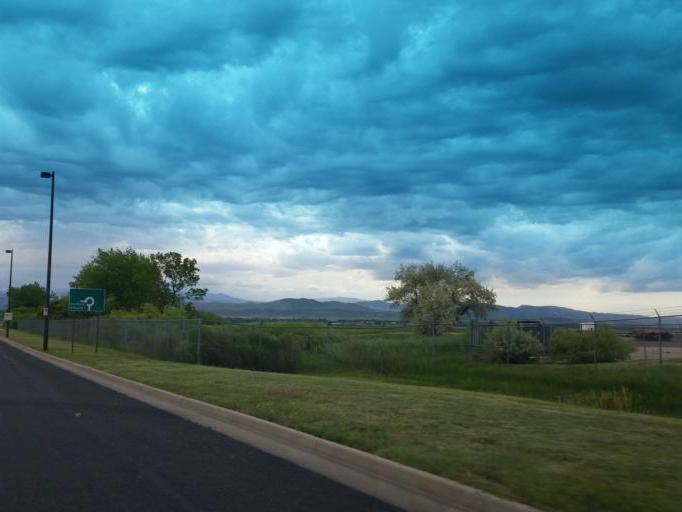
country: US
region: Colorado
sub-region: Larimer County
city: Loveland
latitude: 40.4361
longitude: -104.9989
